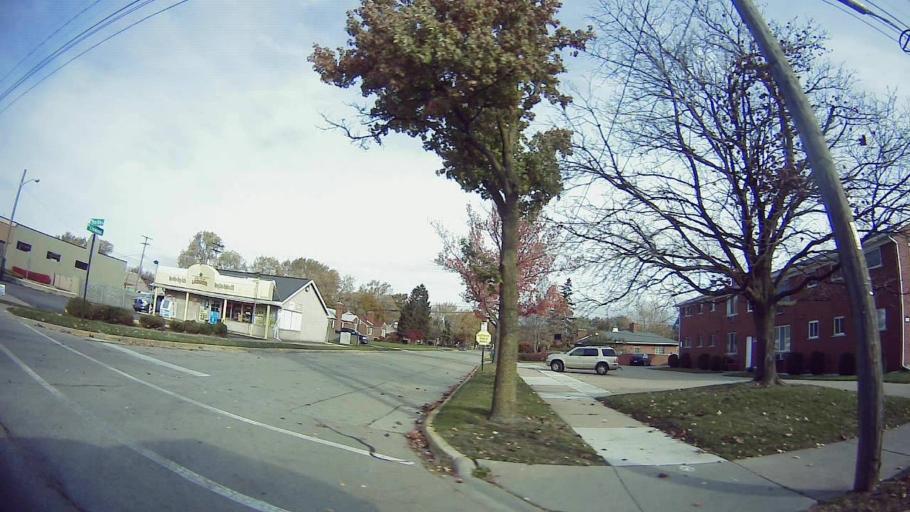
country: US
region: Michigan
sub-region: Macomb County
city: Eastpointe
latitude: 42.4648
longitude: -82.9652
